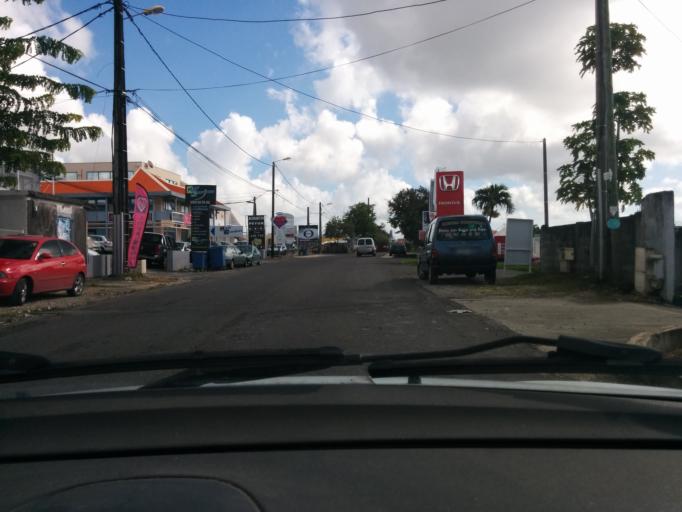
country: GP
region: Guadeloupe
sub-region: Guadeloupe
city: Pointe-a-Pitre
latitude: 16.2419
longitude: -61.5614
